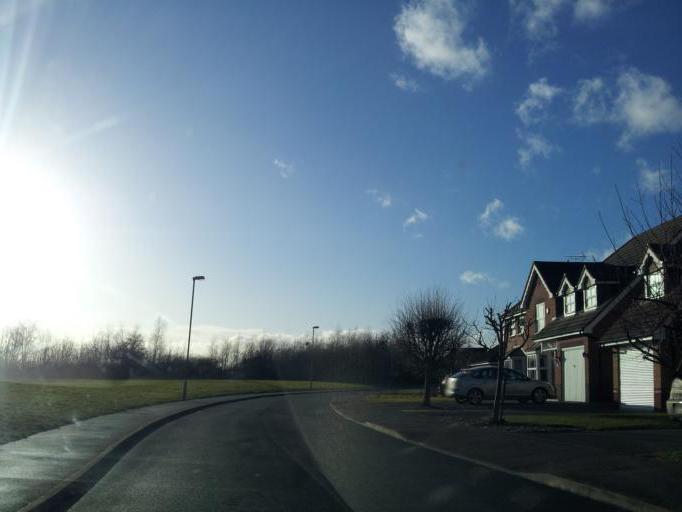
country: GB
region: England
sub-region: Nottinghamshire
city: Newark on Trent
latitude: 53.0734
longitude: -0.7736
